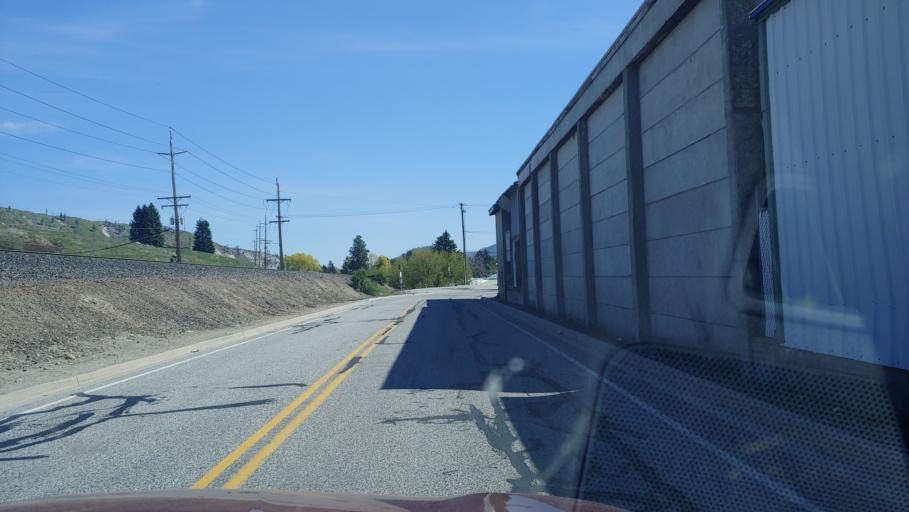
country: US
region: Washington
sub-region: Chelan County
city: Leavenworth
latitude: 47.5722
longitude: -120.6045
